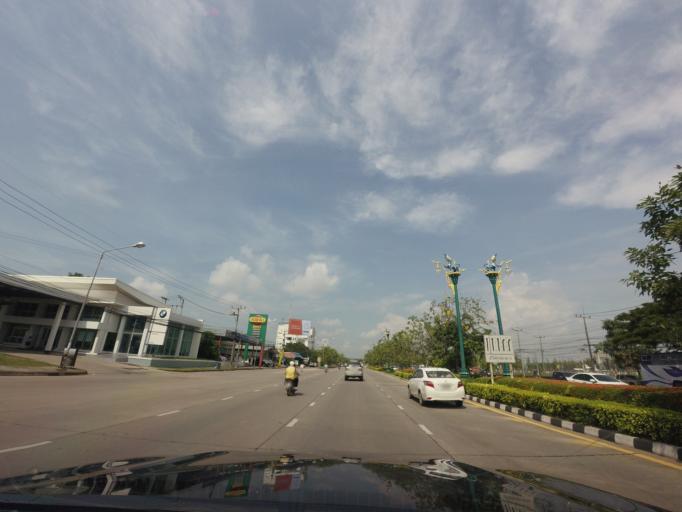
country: TH
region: Khon Kaen
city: Khon Kaen
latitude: 16.4412
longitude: 102.8175
